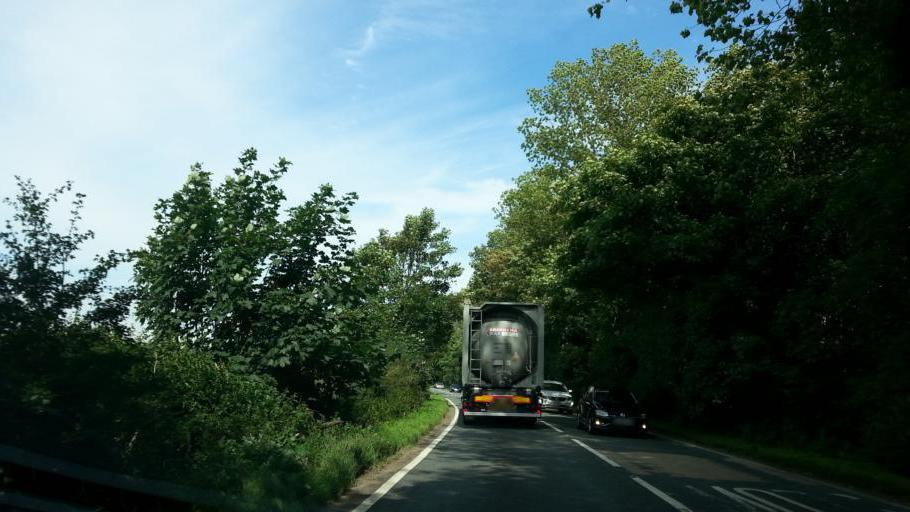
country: GB
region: England
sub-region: Suffolk
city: Exning
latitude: 52.2740
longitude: 0.3935
